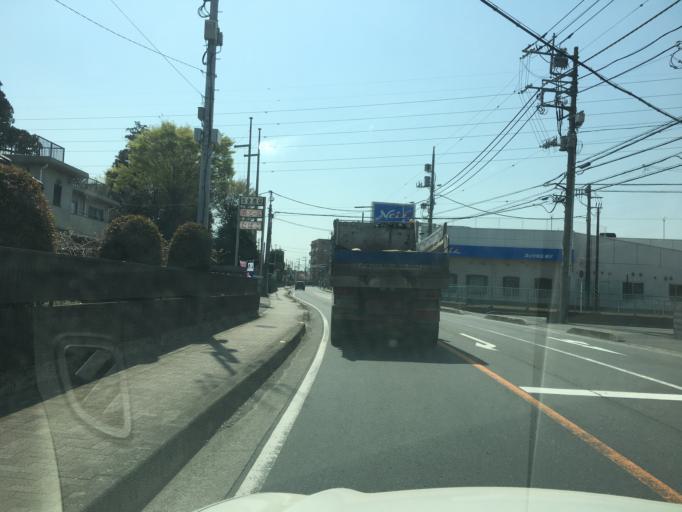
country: JP
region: Saitama
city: Sayama
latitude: 35.8199
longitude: 139.4037
